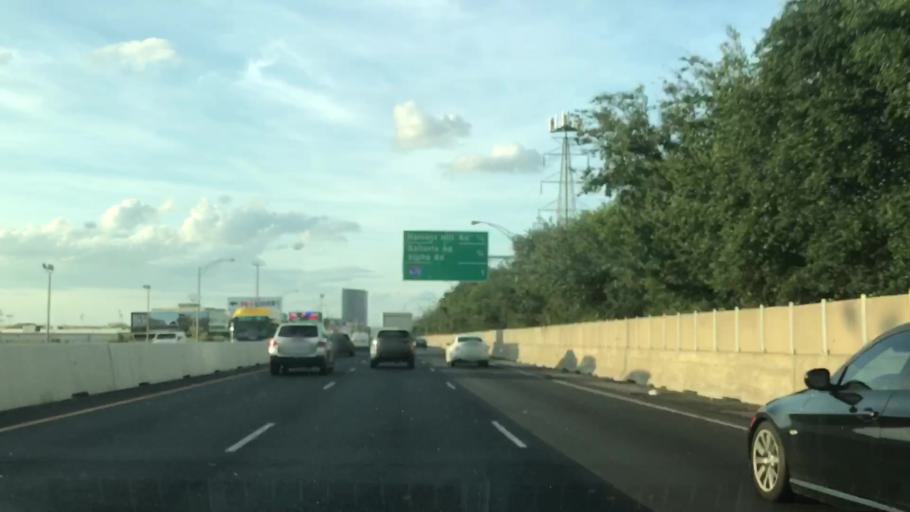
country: US
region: Texas
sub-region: Dallas County
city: Addison
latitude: 32.9109
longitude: -96.8149
